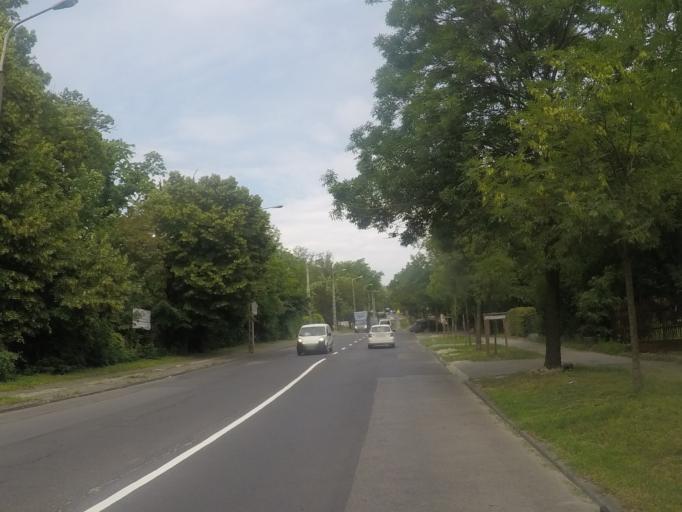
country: HU
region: Budapest
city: Budapest XII. keruelet
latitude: 47.5191
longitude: 18.9810
